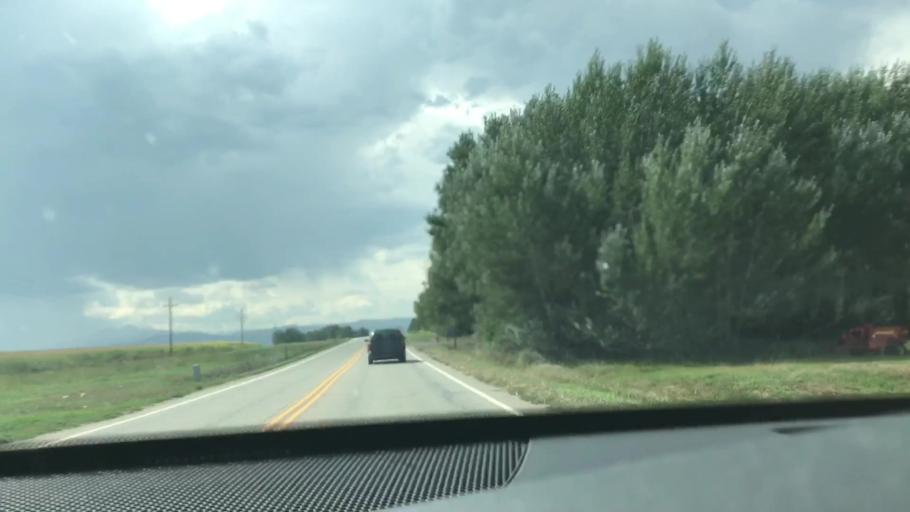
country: US
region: Colorado
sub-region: Larimer County
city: Loveland
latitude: 40.3788
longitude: -105.0067
